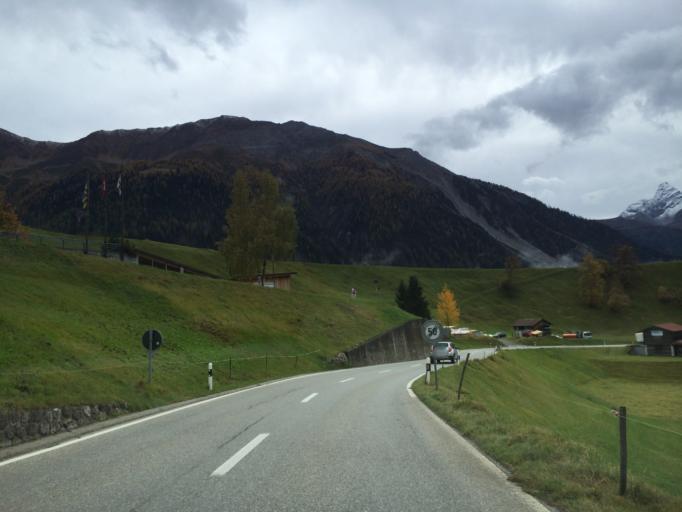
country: CH
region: Grisons
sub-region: Plessur District
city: Arosa
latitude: 46.7042
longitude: 9.7162
